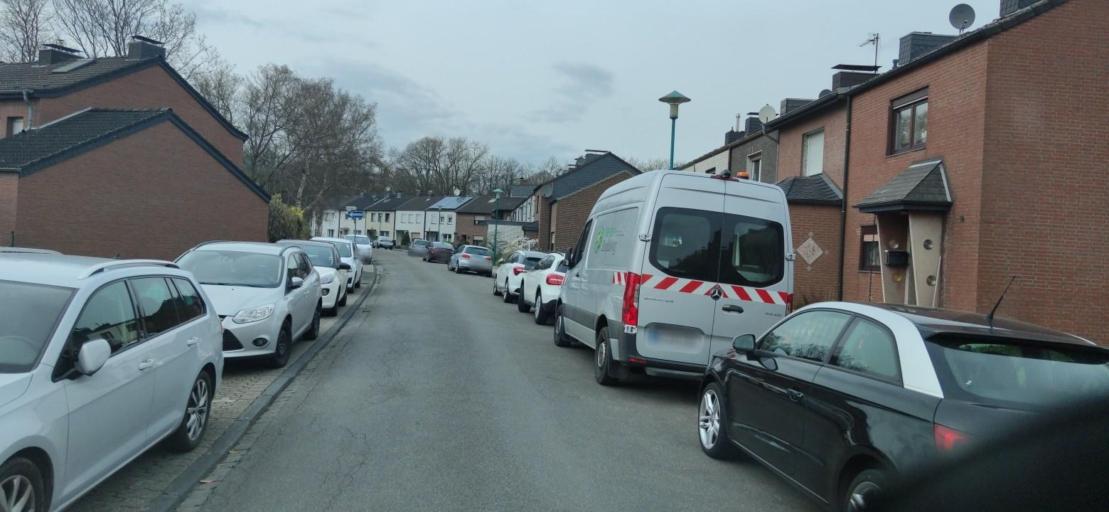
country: DE
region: North Rhine-Westphalia
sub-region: Regierungsbezirk Dusseldorf
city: Dinslaken
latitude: 51.5312
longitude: 6.7504
